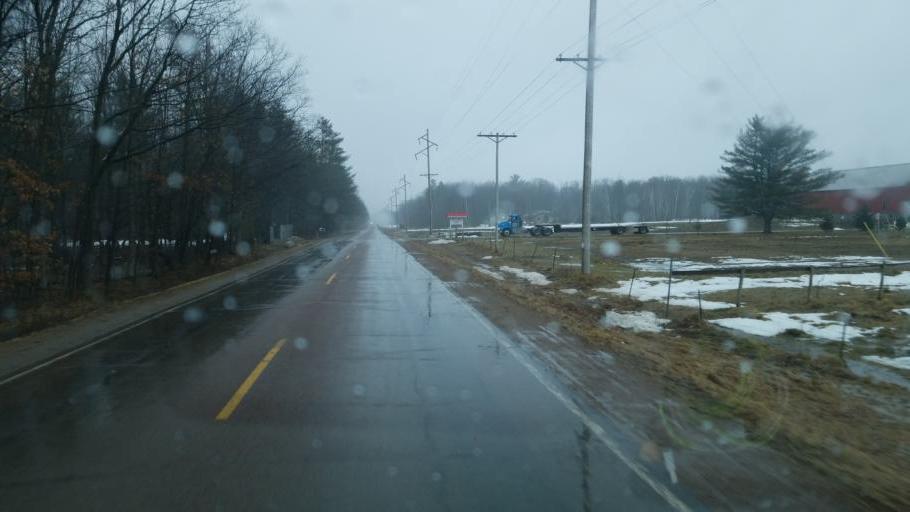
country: US
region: Wisconsin
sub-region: Clark County
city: Neillsville
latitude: 44.5274
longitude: -90.3963
